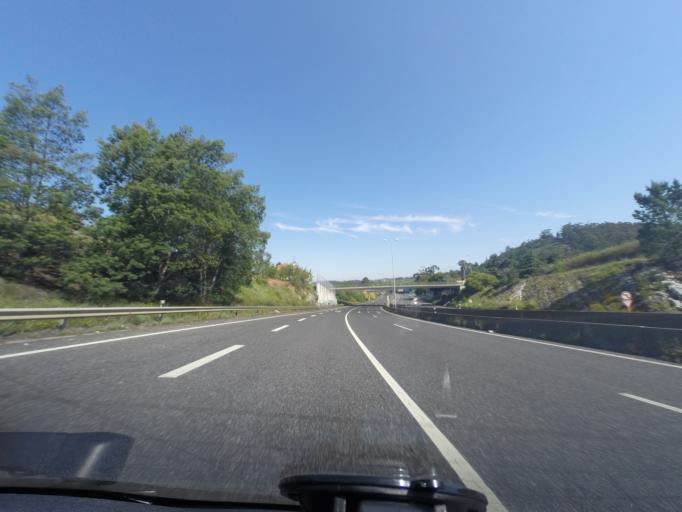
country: PT
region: Lisbon
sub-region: Odivelas
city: Famoes
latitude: 38.7864
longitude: -9.2360
